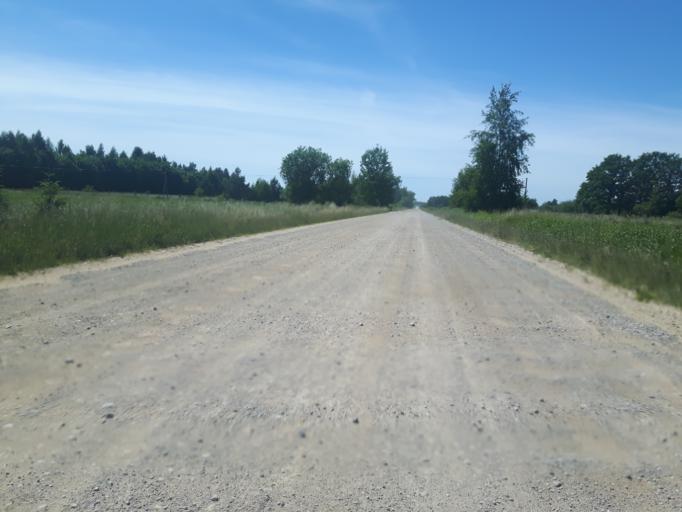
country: LV
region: Grobina
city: Grobina
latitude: 56.5287
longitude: 21.1434
